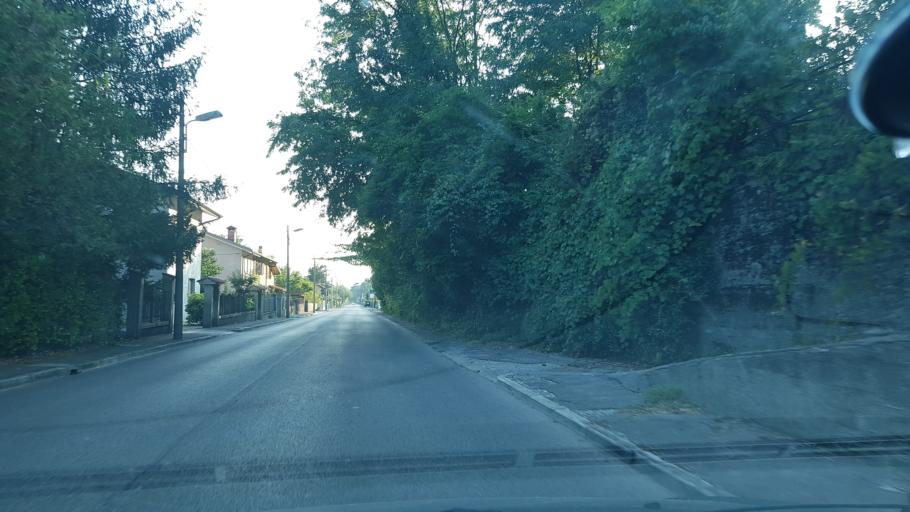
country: IT
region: Friuli Venezia Giulia
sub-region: Provincia di Gorizia
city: Gorizia
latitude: 45.9534
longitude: 13.6064
